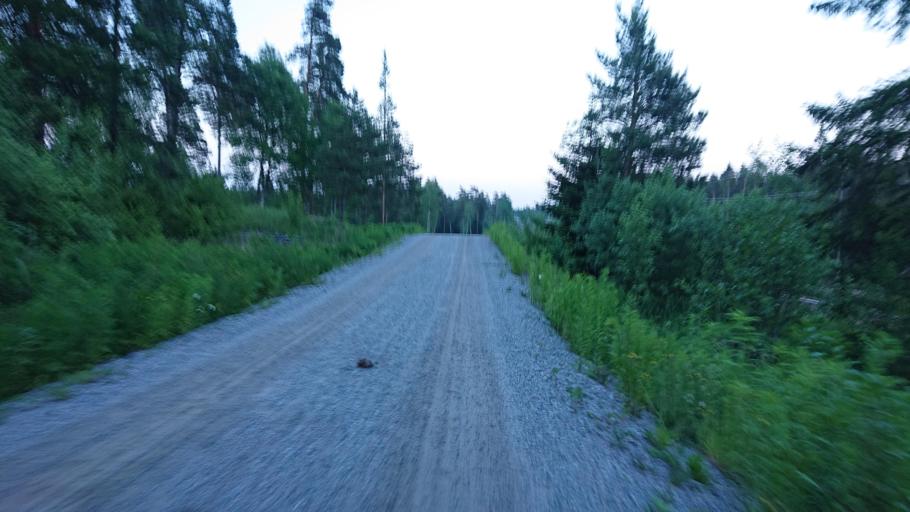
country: SE
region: Stockholm
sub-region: Osterakers Kommun
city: Akersberga
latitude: 59.4697
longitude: 18.2112
